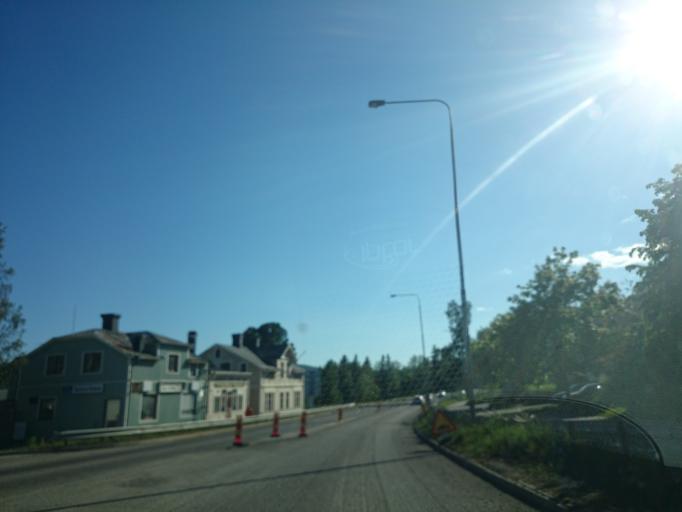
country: SE
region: Vaesternorrland
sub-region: Haernoesands Kommun
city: Haernoesand
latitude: 62.6247
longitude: 17.9266
